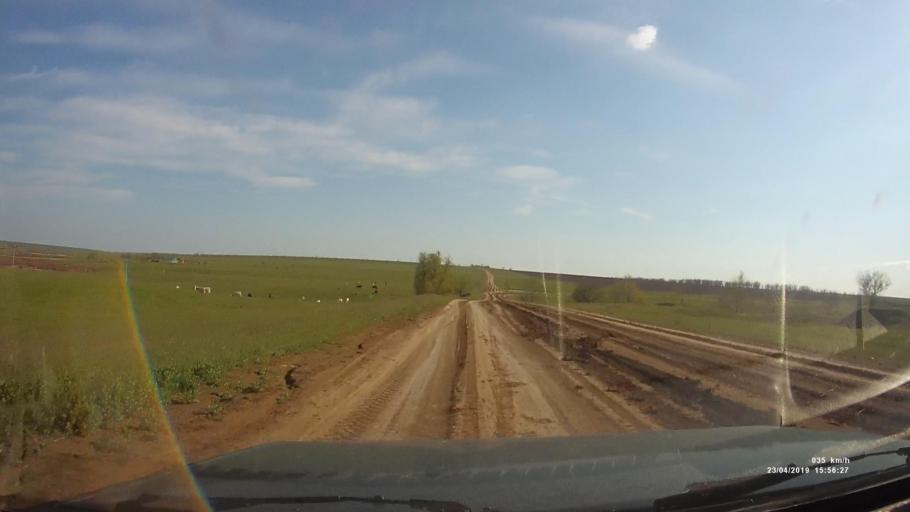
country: RU
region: Rostov
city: Remontnoye
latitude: 46.5370
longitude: 43.1112
